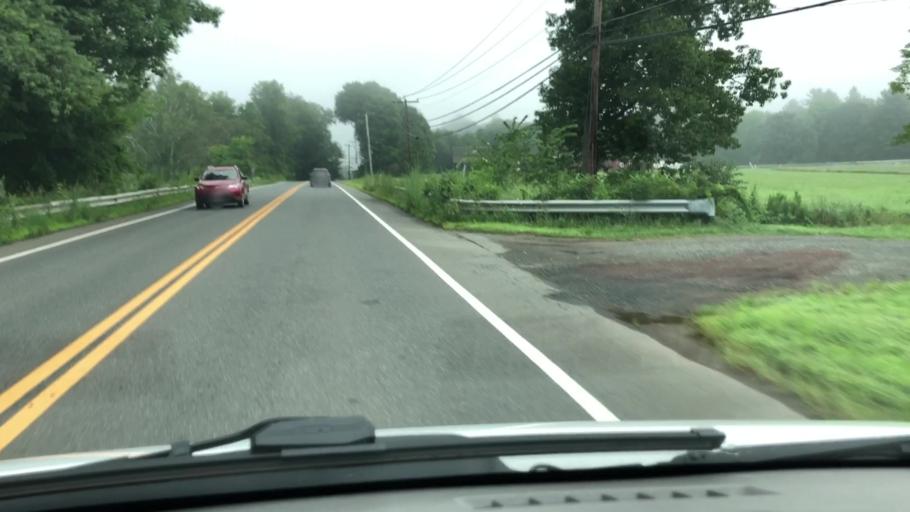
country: US
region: Massachusetts
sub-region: Franklin County
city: South Deerfield
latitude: 42.5107
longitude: -72.6054
